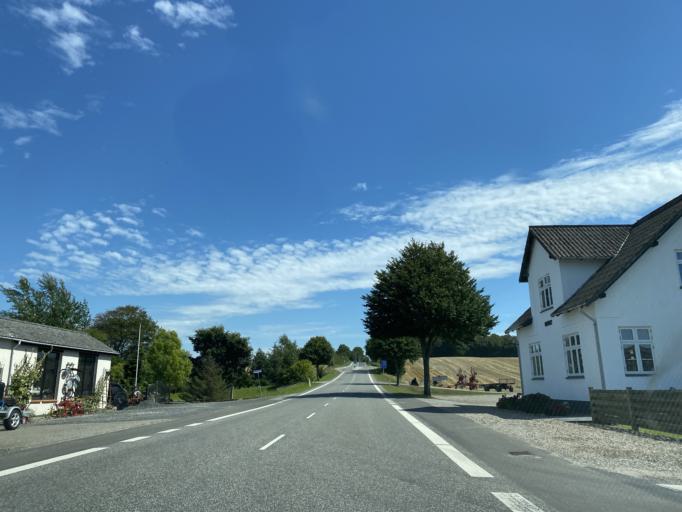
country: DK
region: South Denmark
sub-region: Assens Kommune
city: Harby
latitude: 55.1053
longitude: 10.1114
